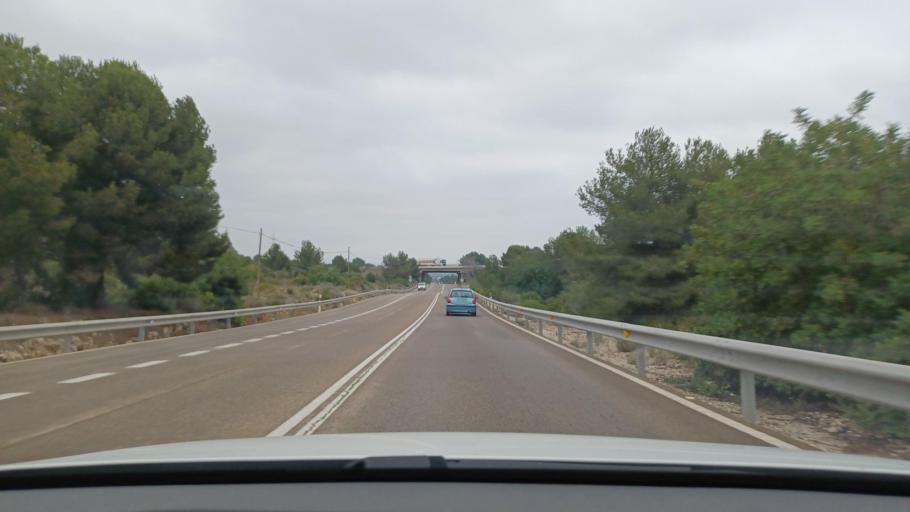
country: ES
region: Valencia
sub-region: Provincia de Castello
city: Orpesa/Oropesa del Mar
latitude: 40.0796
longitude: 0.1159
